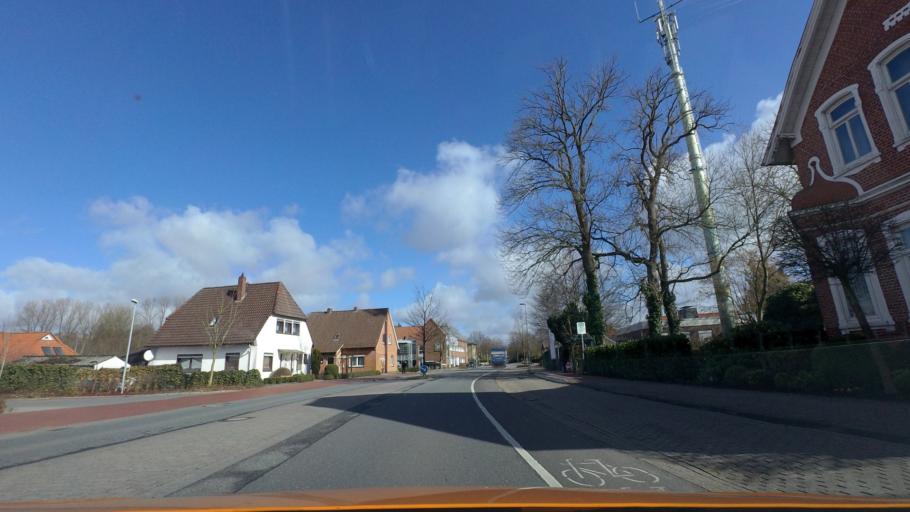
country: DE
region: Lower Saxony
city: Edewecht
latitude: 53.1214
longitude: 7.9762
